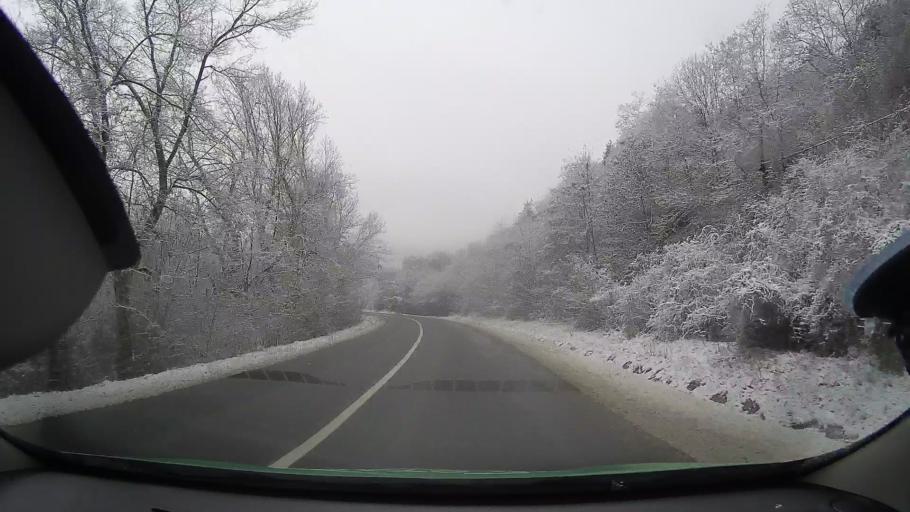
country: RO
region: Cluj
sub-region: Comuna Moldovenesti
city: Moldovenesti
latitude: 46.5101
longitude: 23.6587
